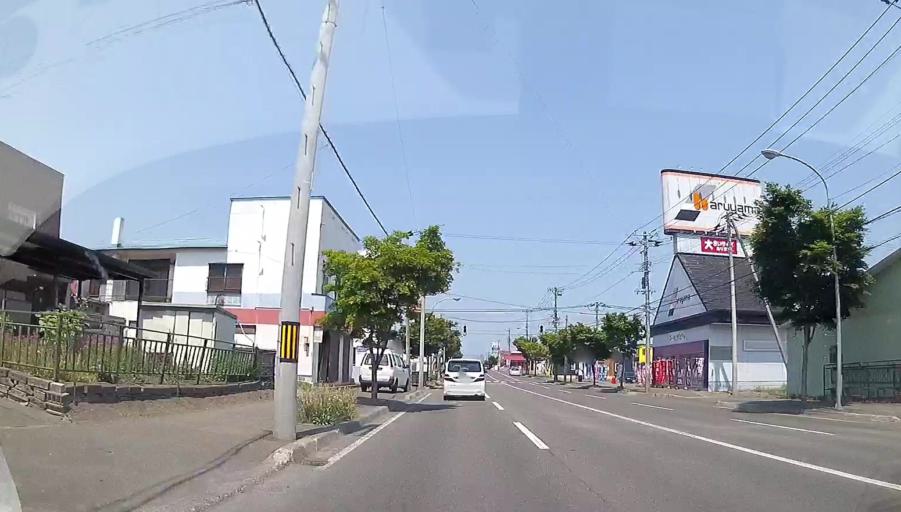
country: JP
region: Hokkaido
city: Obihiro
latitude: 42.8935
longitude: 143.2011
